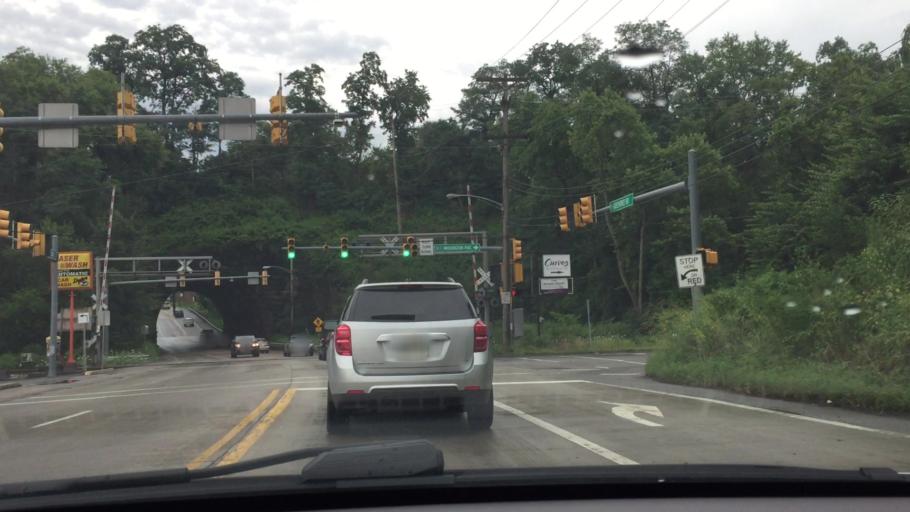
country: US
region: Pennsylvania
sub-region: Allegheny County
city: Heidelberg
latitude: 40.3866
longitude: -80.0891
